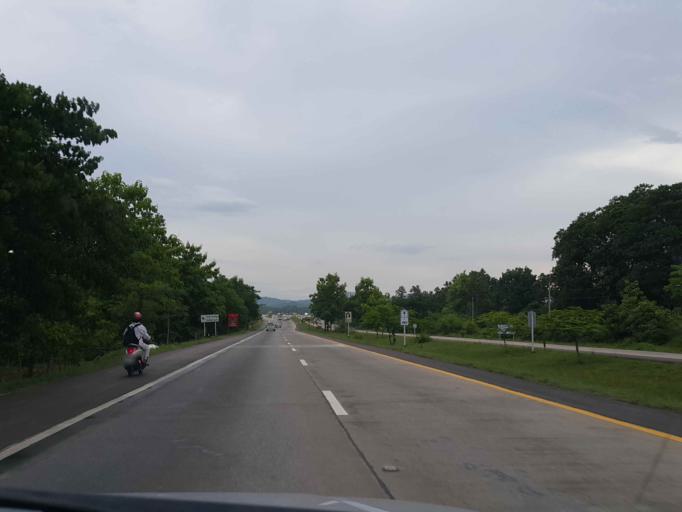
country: TH
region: Lampang
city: Hang Chat
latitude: 18.3236
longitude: 99.2939
